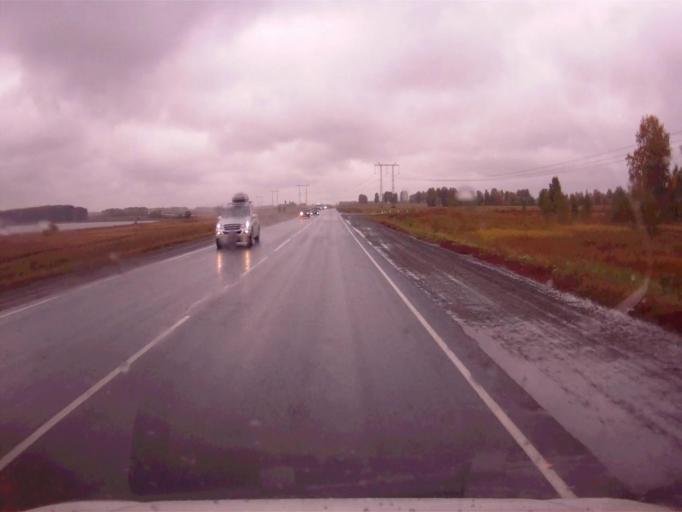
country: RU
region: Chelyabinsk
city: Roshchino
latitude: 55.3888
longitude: 61.1266
